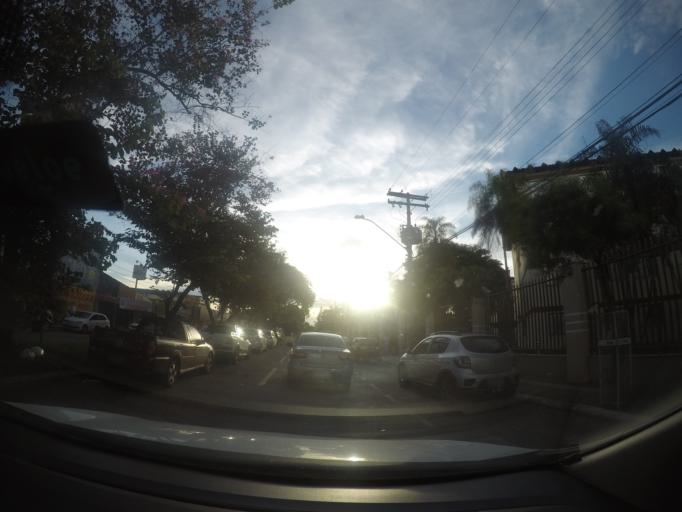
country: BR
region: Goias
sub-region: Goiania
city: Goiania
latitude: -16.6851
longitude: -49.3146
